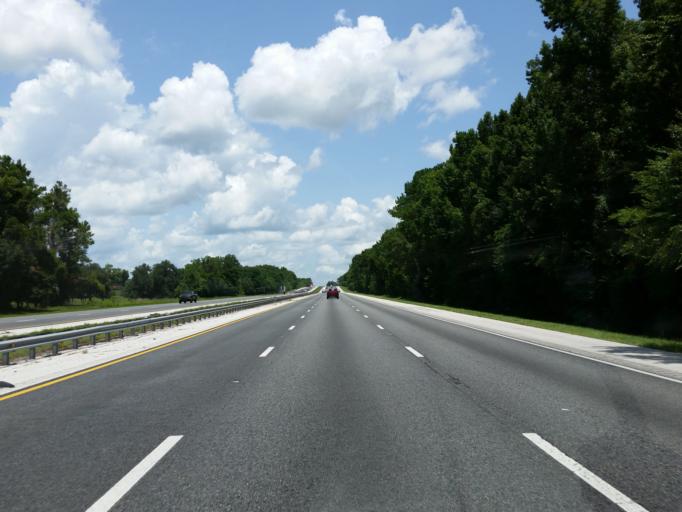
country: US
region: Florida
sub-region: Marion County
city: Citra
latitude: 29.3386
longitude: -82.2165
